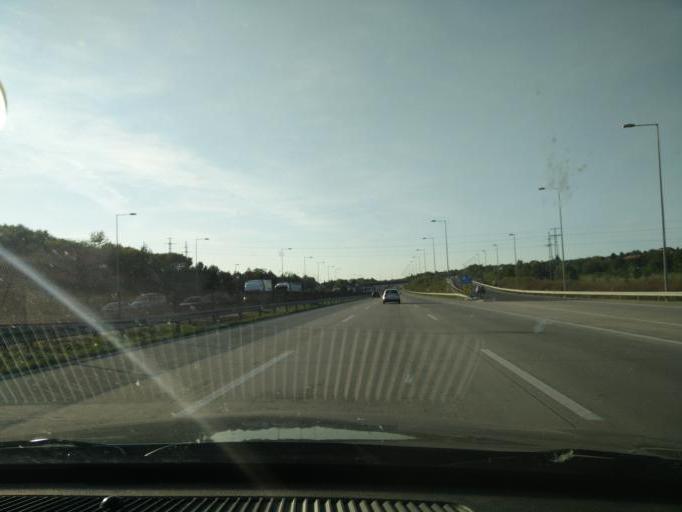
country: HU
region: Pest
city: Diosd
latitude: 47.4087
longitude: 18.9639
